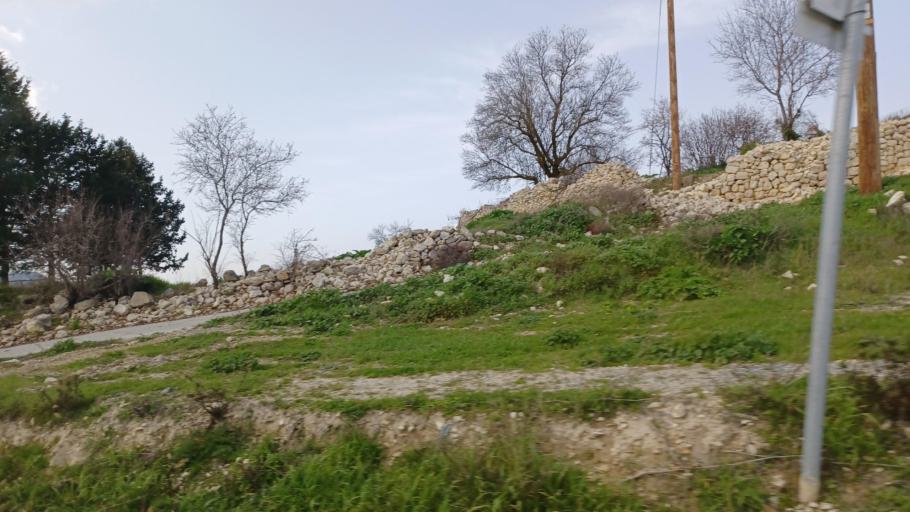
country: CY
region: Limassol
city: Pachna
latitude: 34.7845
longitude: 32.7377
